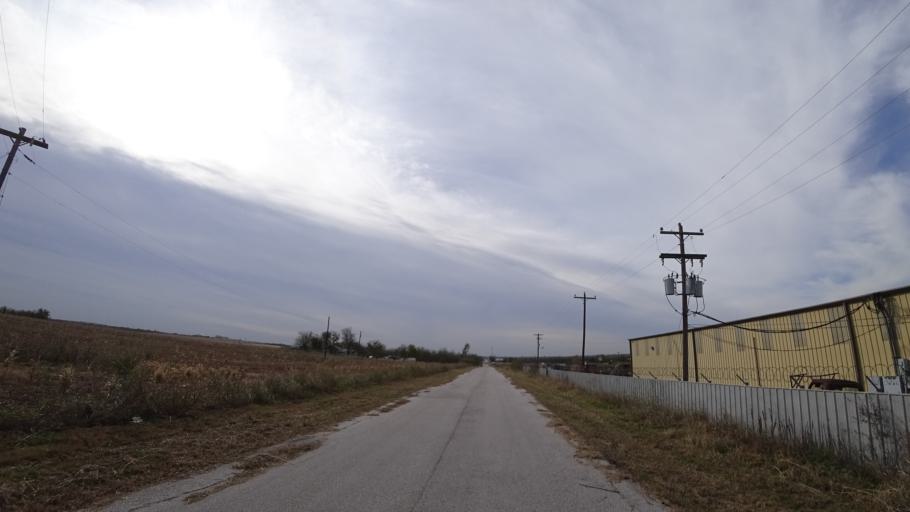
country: US
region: Texas
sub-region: Travis County
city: Onion Creek
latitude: 30.1550
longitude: -97.6939
